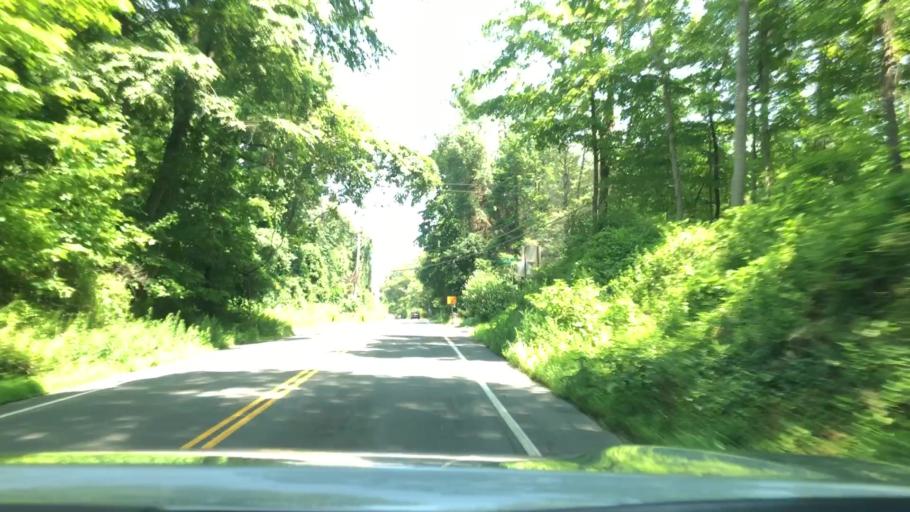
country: US
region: New York
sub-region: Orange County
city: Fort Montgomery
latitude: 41.3352
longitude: -73.9587
